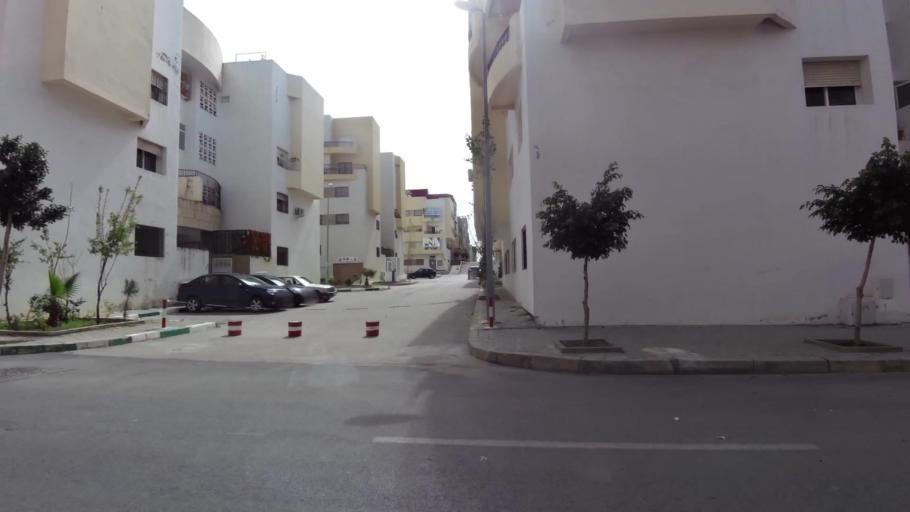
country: MA
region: Tanger-Tetouan
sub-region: Tanger-Assilah
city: Tangier
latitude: 35.7441
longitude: -5.8408
